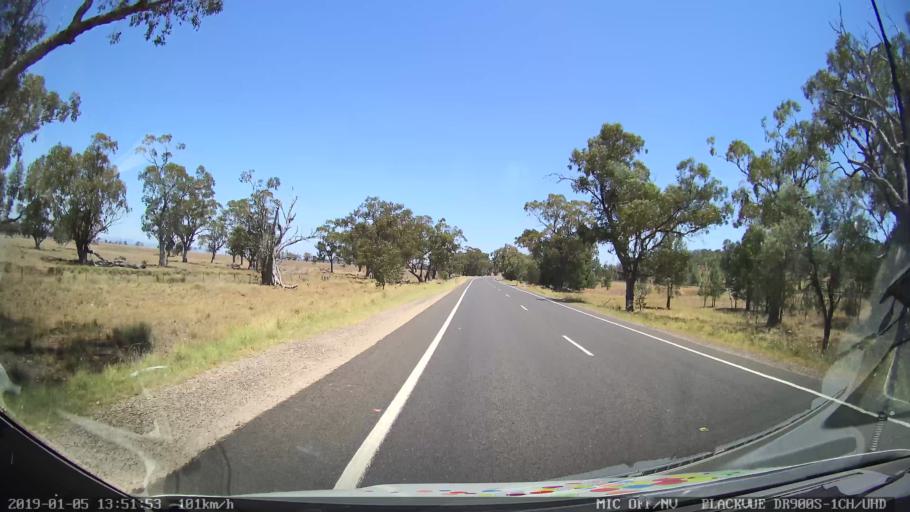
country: AU
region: New South Wales
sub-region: Gunnedah
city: Gunnedah
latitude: -31.0514
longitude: 150.2777
